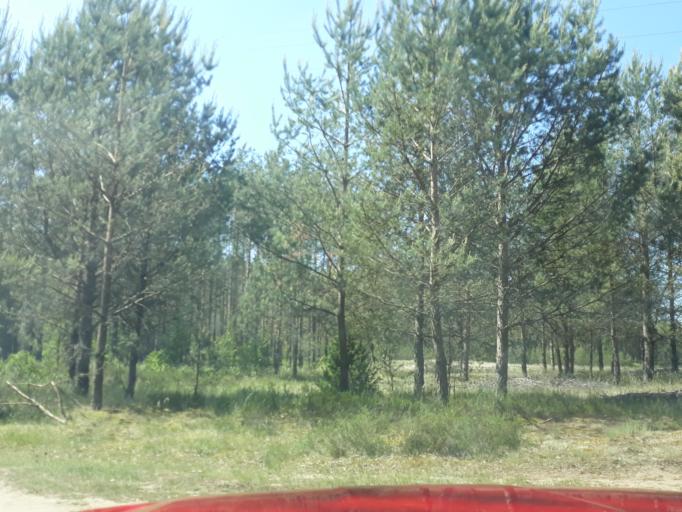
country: PL
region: Pomeranian Voivodeship
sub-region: Powiat chojnicki
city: Chojnice
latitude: 53.8729
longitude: 17.5390
